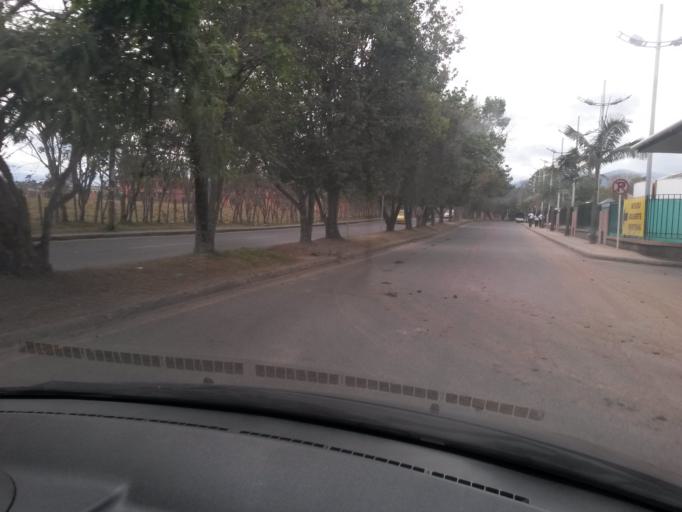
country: CO
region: Cauca
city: Popayan
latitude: 2.4604
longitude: -76.5955
